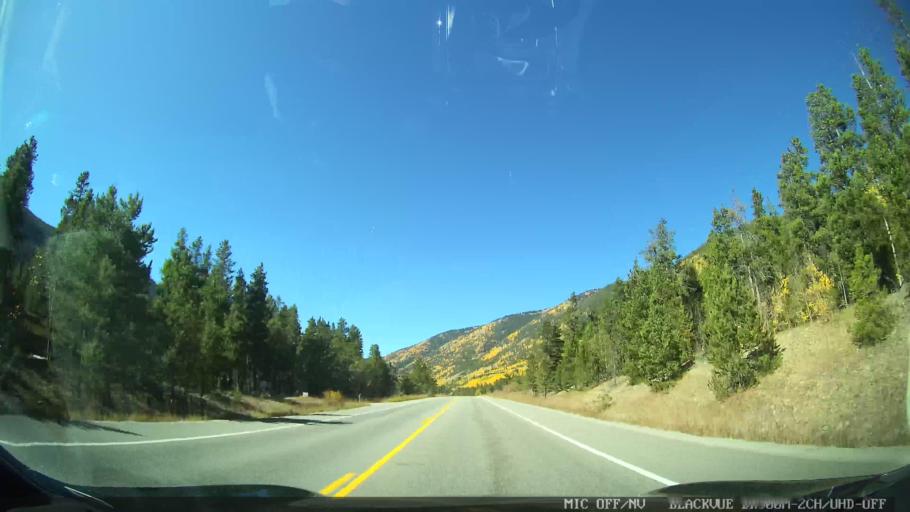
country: US
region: Colorado
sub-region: Lake County
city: Leadville
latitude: 39.3093
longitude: -106.2432
